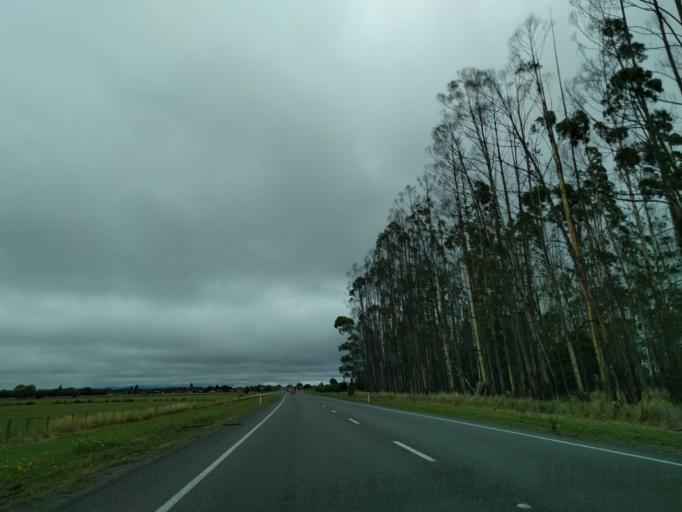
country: NZ
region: Canterbury
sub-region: Waimakariri District
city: Kaiapoi
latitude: -43.3637
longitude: 172.6516
